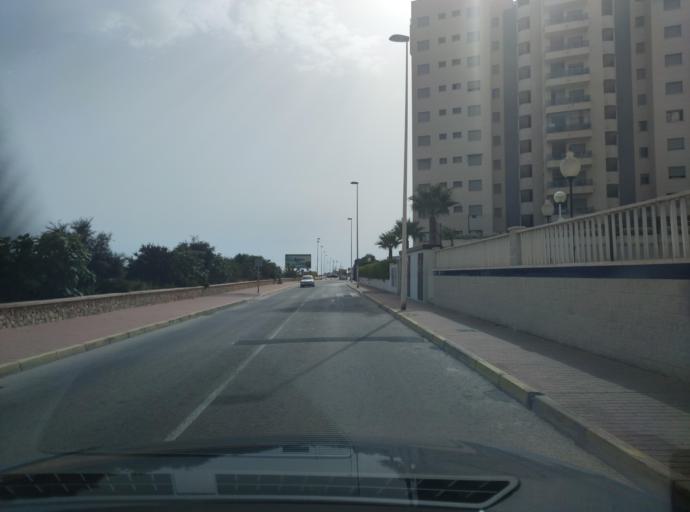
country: ES
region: Valencia
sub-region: Provincia de Alicante
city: Guardamar del Segura
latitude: 38.1093
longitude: -0.6502
